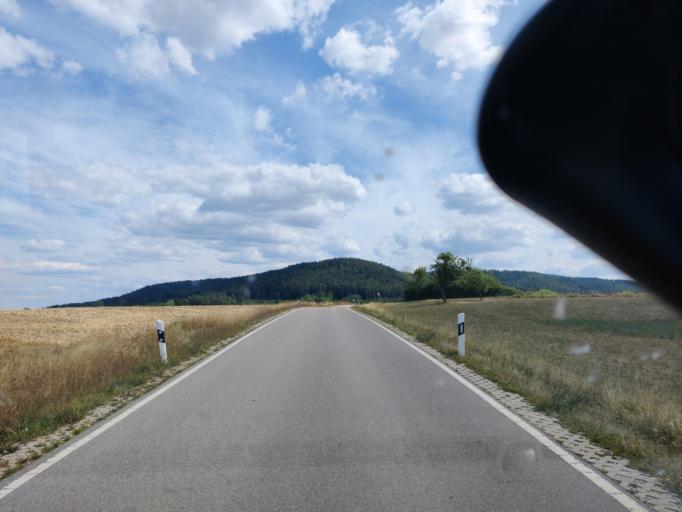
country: DE
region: Bavaria
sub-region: Regierungsbezirk Mittelfranken
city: Bergen
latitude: 49.0968
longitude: 11.1412
